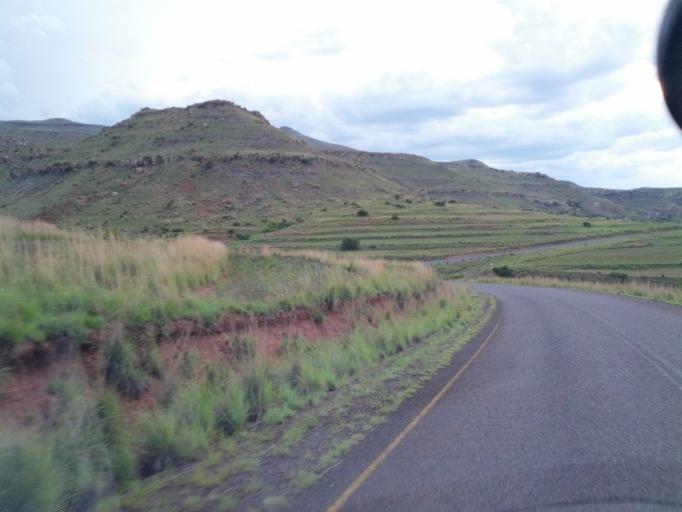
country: LS
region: Qacha's Nek
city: Qacha's Nek
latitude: -30.0667
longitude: 28.5508
